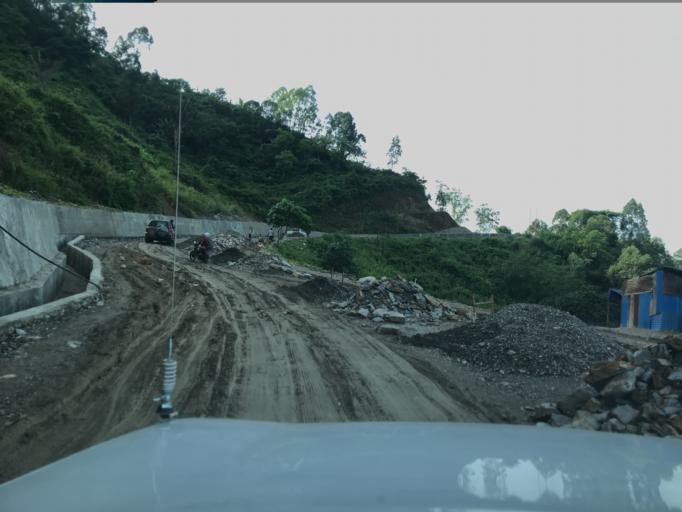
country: TL
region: Aileu
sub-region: Aileu Villa
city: Aileu
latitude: -8.6542
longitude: 125.5276
